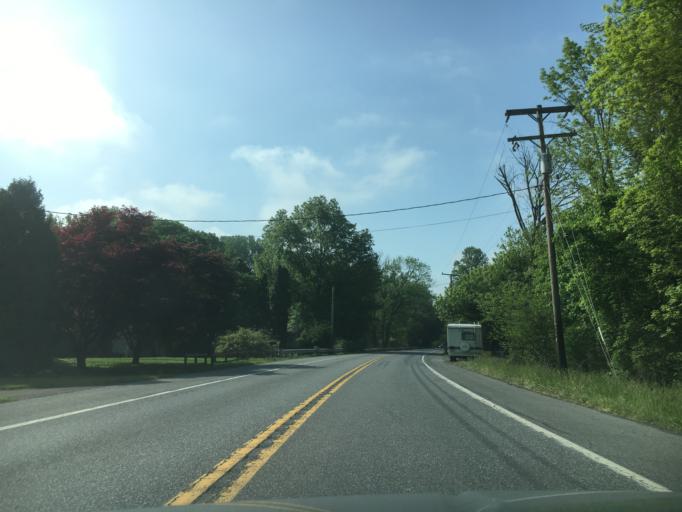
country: US
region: Pennsylvania
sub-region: Berks County
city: New Berlinville
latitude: 40.3594
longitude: -75.6662
